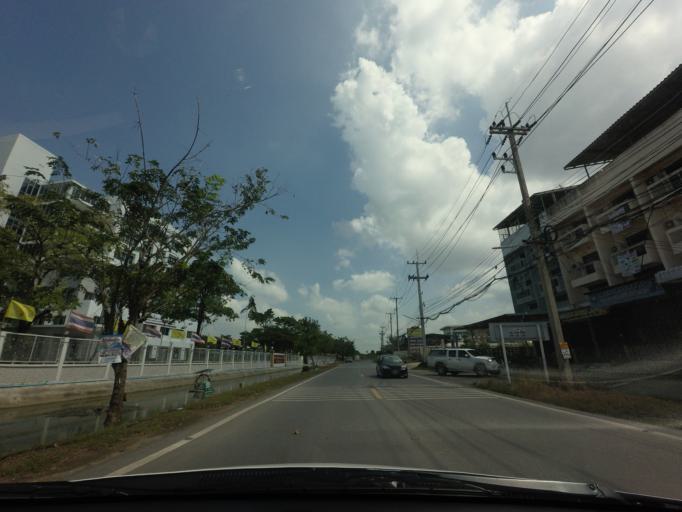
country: TH
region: Nakhon Pathom
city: Nakhon Chai Si
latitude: 13.8030
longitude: 100.1897
